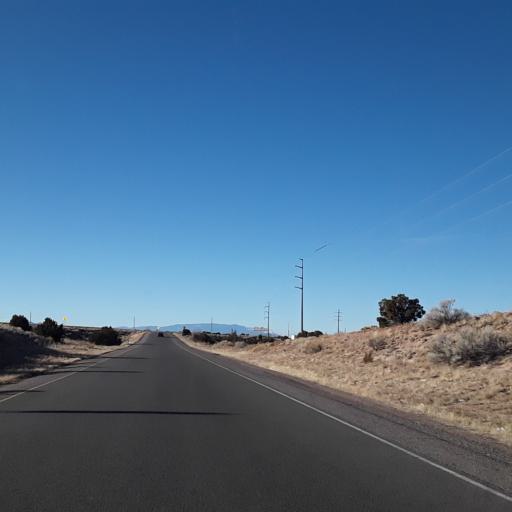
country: US
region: New Mexico
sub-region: Santa Fe County
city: Santa Fe
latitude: 35.6361
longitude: -105.9582
